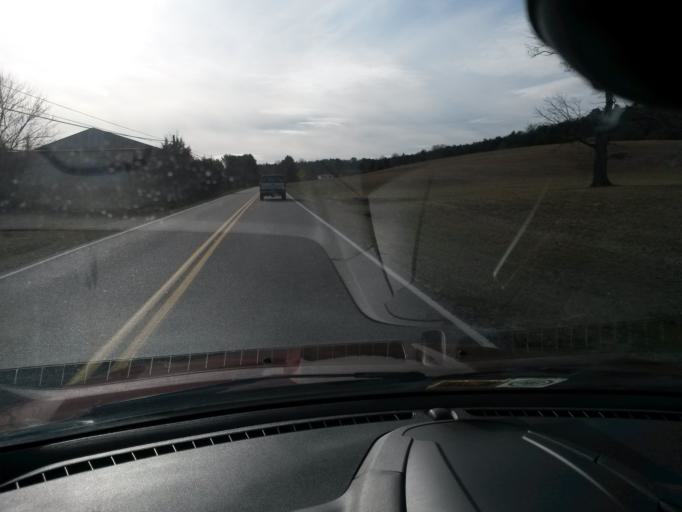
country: US
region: Virginia
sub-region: Rockbridge County
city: East Lexington
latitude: 38.0331
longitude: -79.4453
